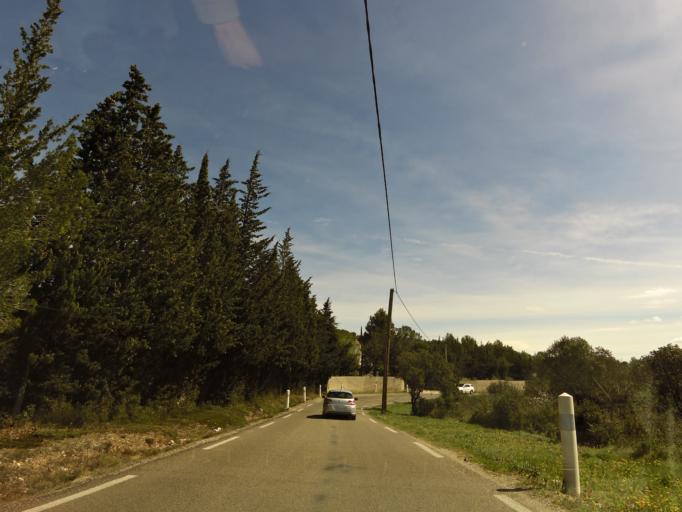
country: FR
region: Languedoc-Roussillon
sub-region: Departement du Gard
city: Bernis
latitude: 43.7832
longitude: 4.2698
